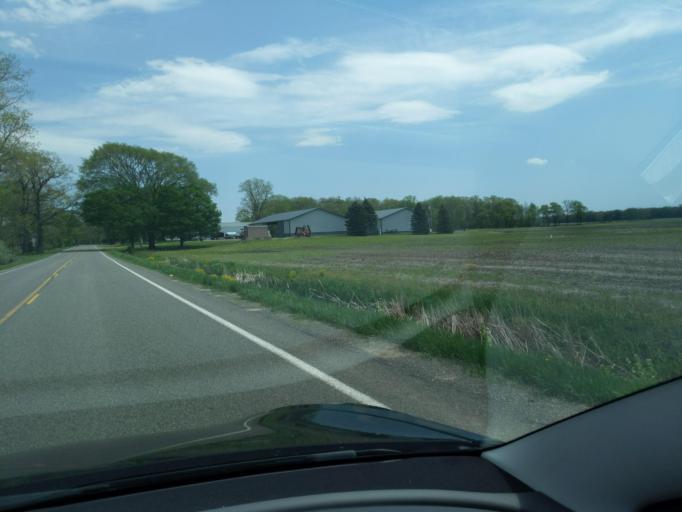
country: US
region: Michigan
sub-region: Ingham County
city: Stockbridge
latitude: 42.4825
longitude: -84.2770
